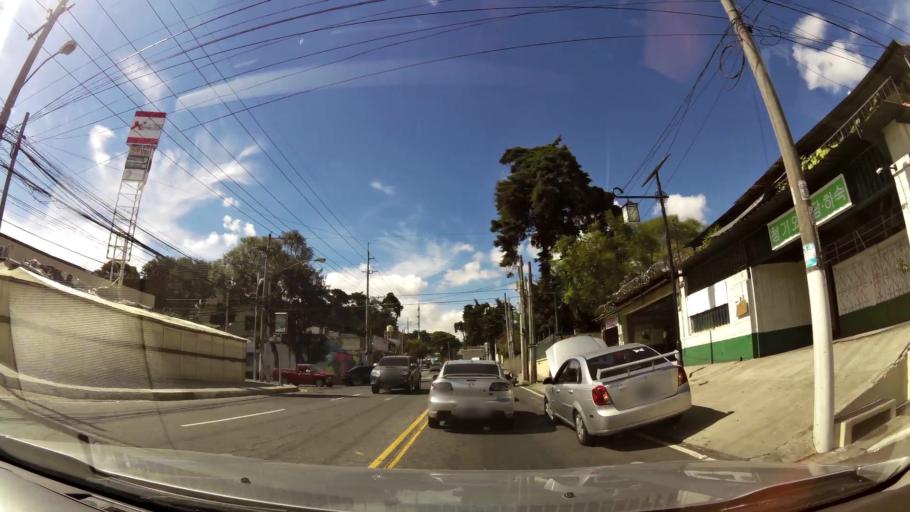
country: GT
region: Guatemala
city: Mixco
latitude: 14.6337
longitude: -90.5651
